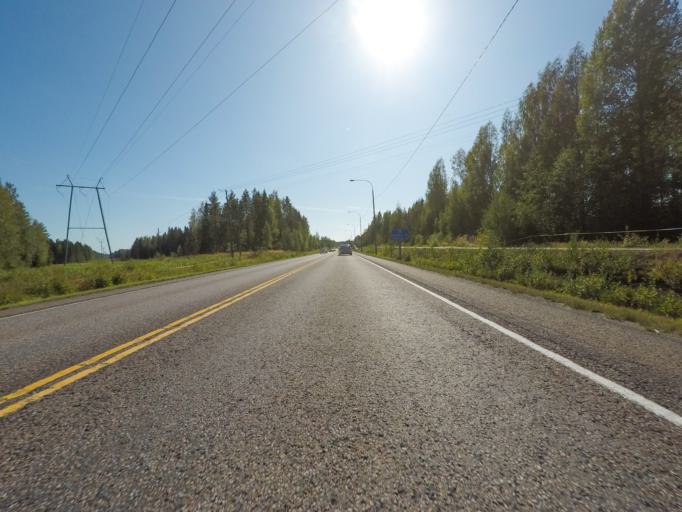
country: FI
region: Northern Savo
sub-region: Varkaus
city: Varkaus
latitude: 62.3980
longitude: 27.8212
